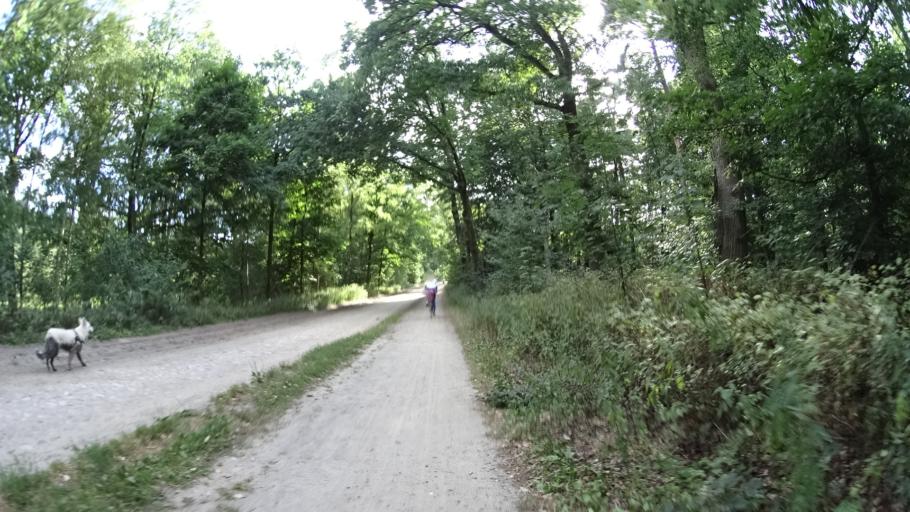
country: DE
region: Lower Saxony
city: Undeloh
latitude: 53.1511
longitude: 9.9176
